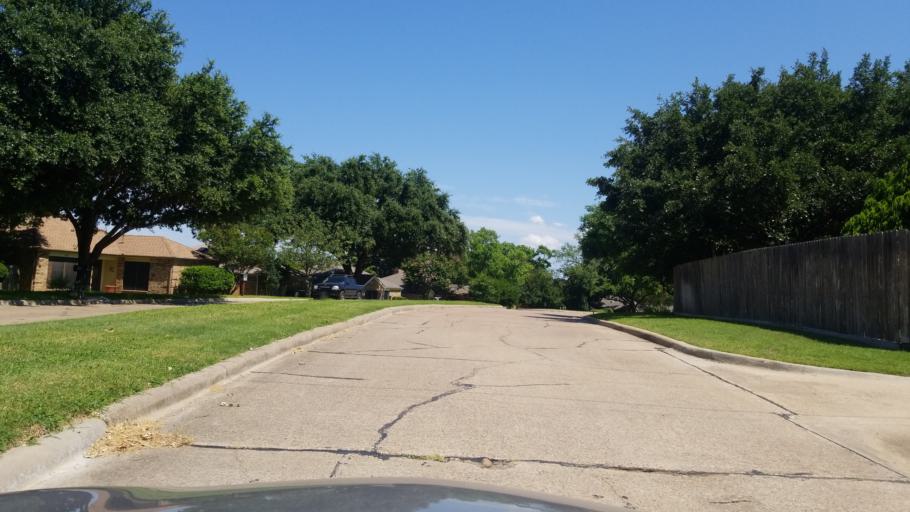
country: US
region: Texas
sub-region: Dallas County
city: Grand Prairie
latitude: 32.6913
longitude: -96.9938
